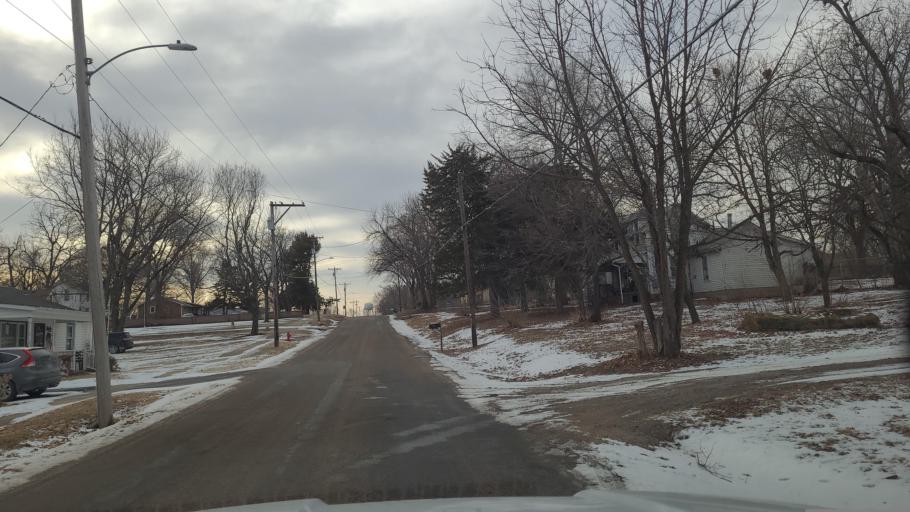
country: US
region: Kansas
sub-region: Douglas County
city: Lawrence
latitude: 39.0413
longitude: -95.3970
